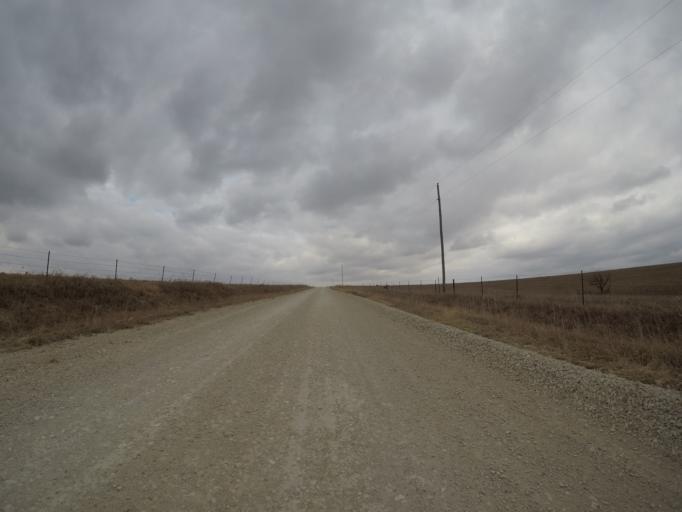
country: US
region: Kansas
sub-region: Morris County
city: Council Grove
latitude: 38.7556
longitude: -96.2794
